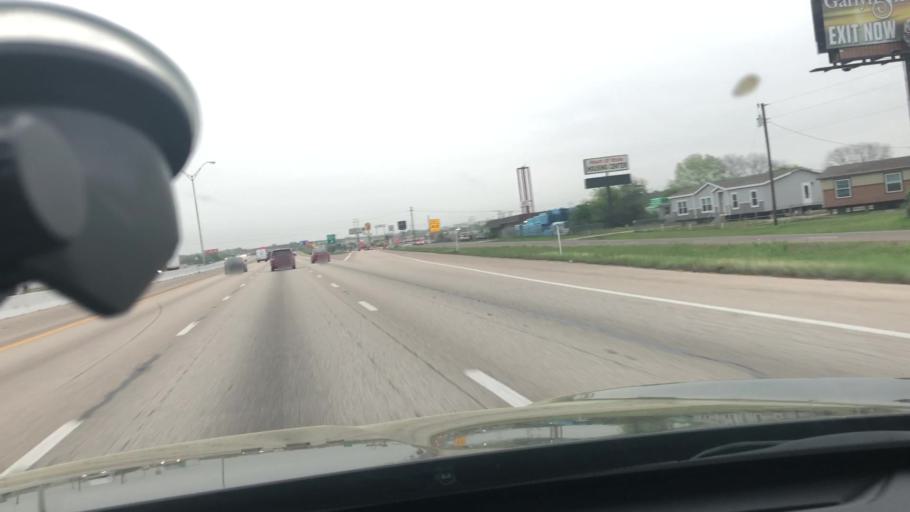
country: US
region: Texas
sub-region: Bell County
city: Belton
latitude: 31.0761
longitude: -97.4172
